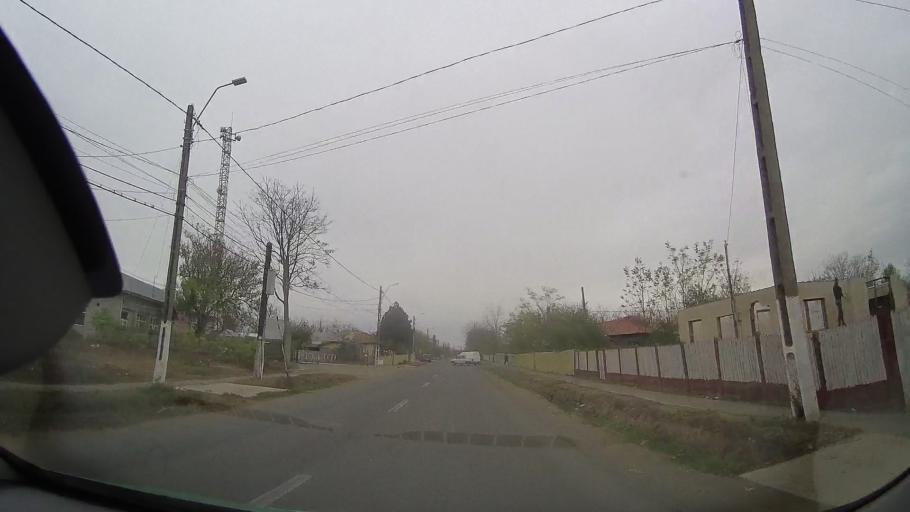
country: RO
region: Braila
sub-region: Comuna Budesti
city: Tataru
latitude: 44.8477
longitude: 27.4289
